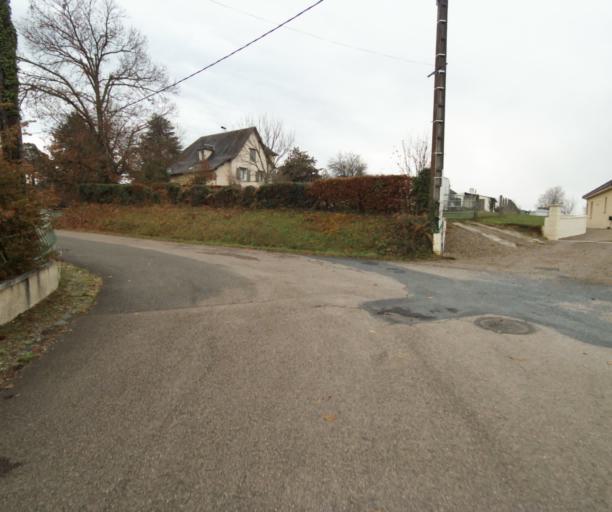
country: FR
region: Limousin
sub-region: Departement de la Correze
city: Tulle
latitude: 45.2667
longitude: 1.7306
